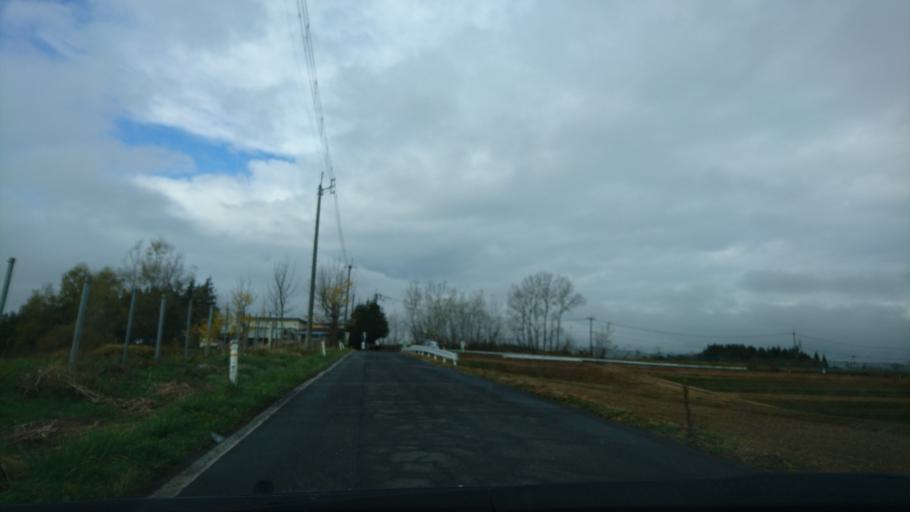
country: JP
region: Iwate
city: Ichinoseki
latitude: 38.8876
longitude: 141.1928
